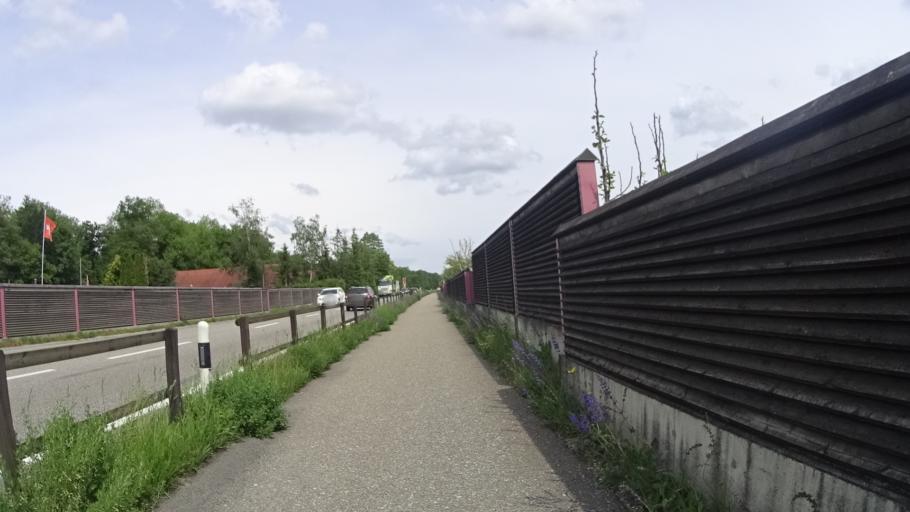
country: CH
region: Aargau
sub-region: Bezirk Rheinfelden
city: Rheinfelden
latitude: 47.5523
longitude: 7.8078
